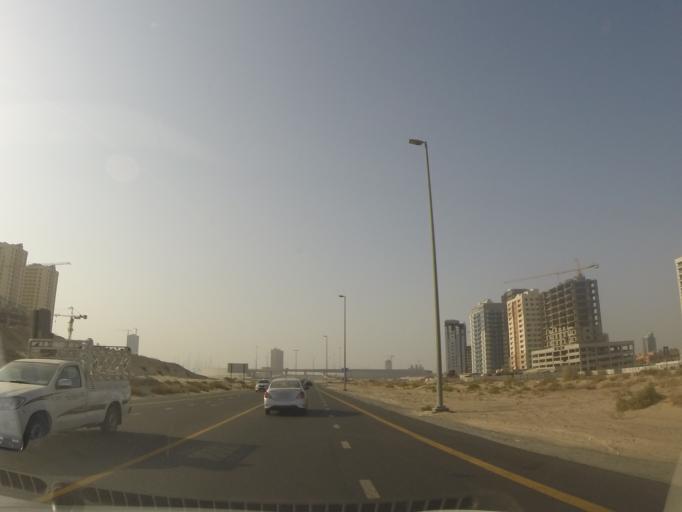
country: AE
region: Dubai
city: Dubai
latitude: 25.0414
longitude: 55.2014
